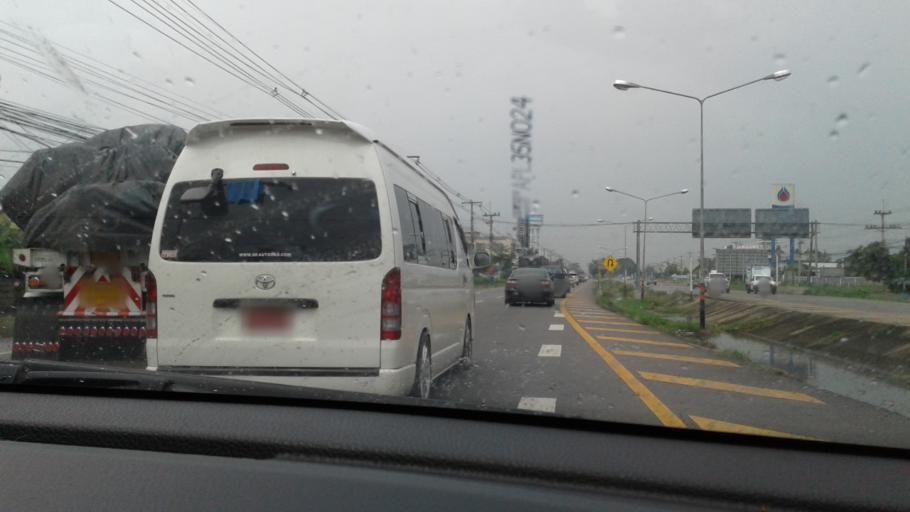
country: TH
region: Prachuap Khiri Khan
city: Kui Buri
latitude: 12.0699
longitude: 99.8594
